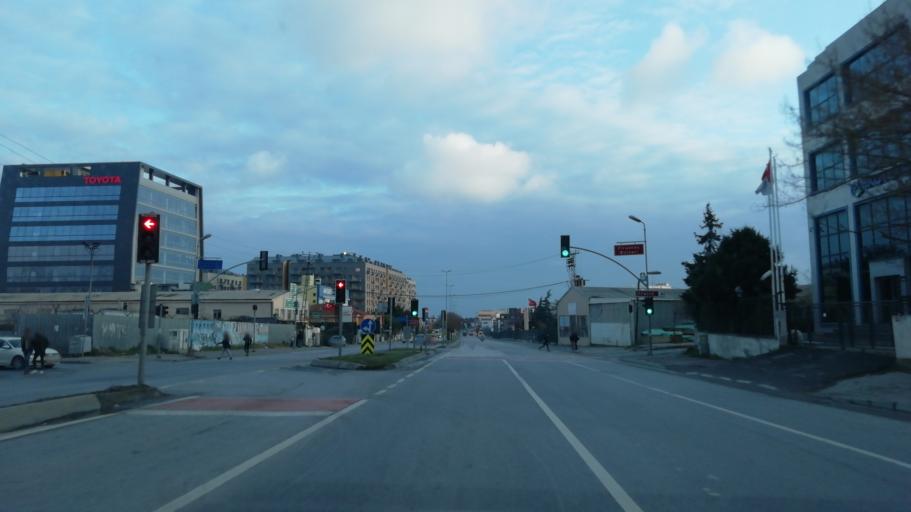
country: TR
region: Istanbul
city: Yakuplu
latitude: 40.9948
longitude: 28.7157
